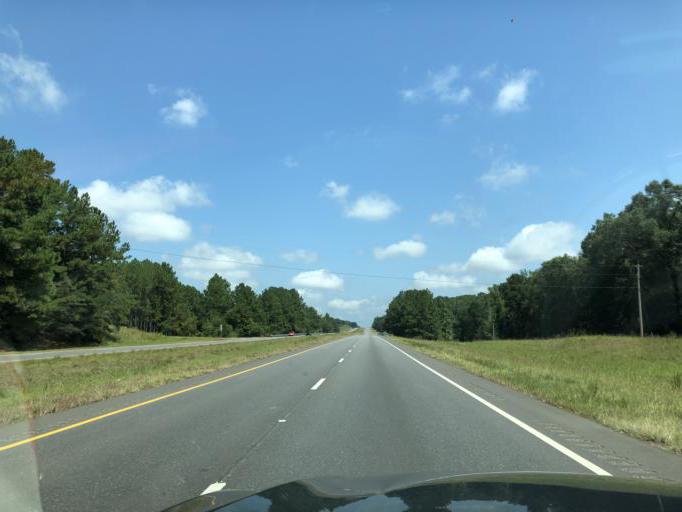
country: US
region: Alabama
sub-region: Henry County
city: Abbeville
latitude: 31.4675
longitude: -85.3051
